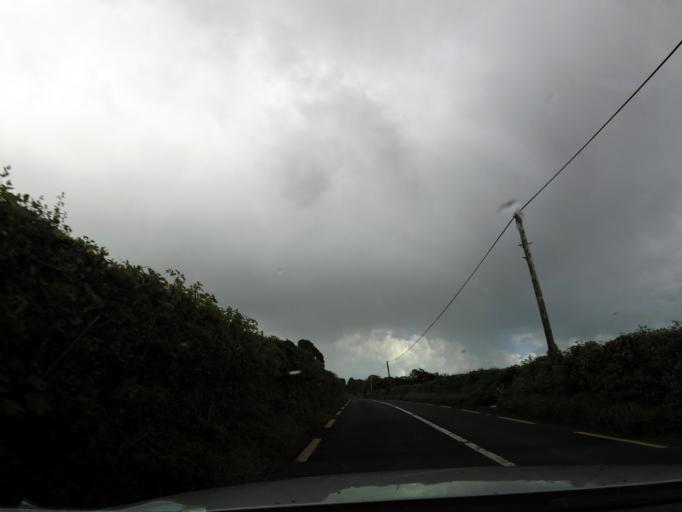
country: IE
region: Munster
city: Thurles
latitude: 52.7016
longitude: -7.8225
